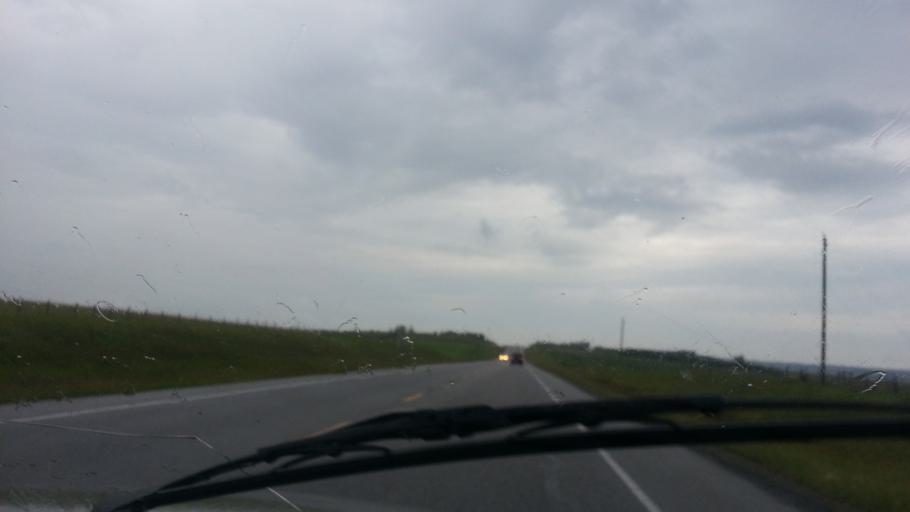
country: CA
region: Alberta
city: Cochrane
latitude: 51.1350
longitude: -114.4667
